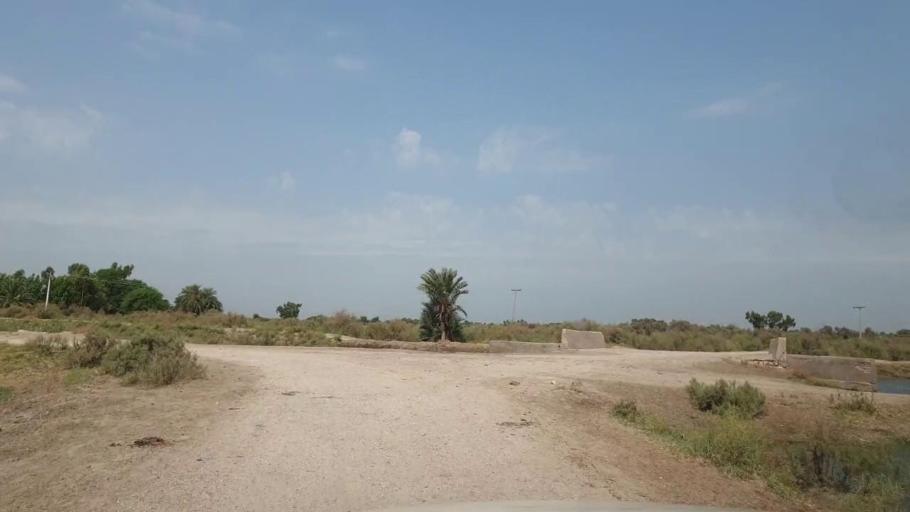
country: PK
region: Sindh
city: Ratodero
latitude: 27.8395
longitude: 68.2490
